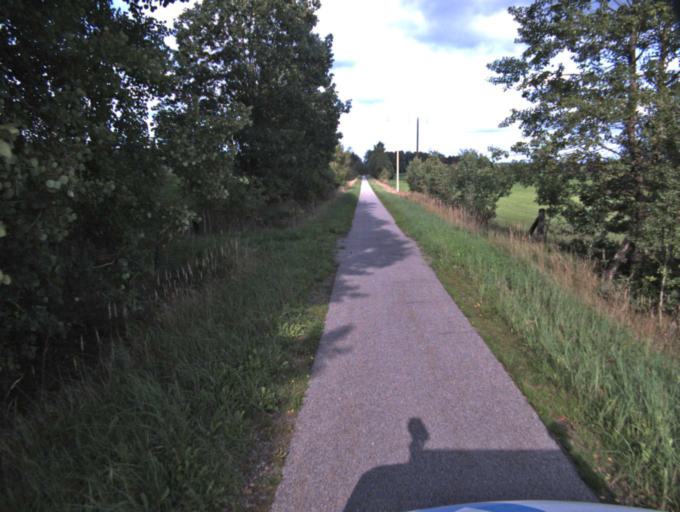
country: SE
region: Vaestra Goetaland
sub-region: Ulricehamns Kommun
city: Ulricehamn
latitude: 57.8933
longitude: 13.4412
